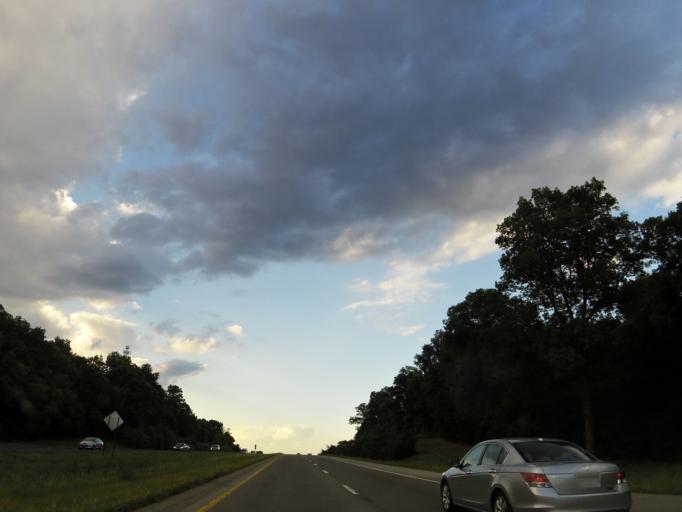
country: US
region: Tennessee
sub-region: Maury County
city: Spring Hill
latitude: 35.6829
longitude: -86.8874
